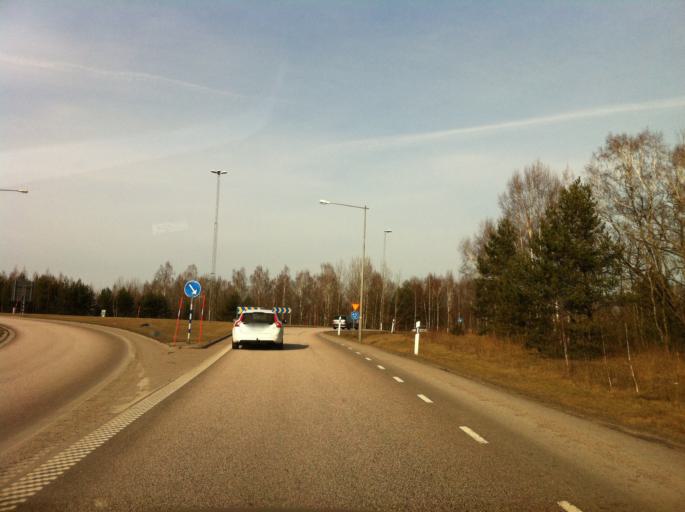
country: SE
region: Vaestra Goetaland
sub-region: Skovde Kommun
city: Skoevde
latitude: 58.4193
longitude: 13.8862
